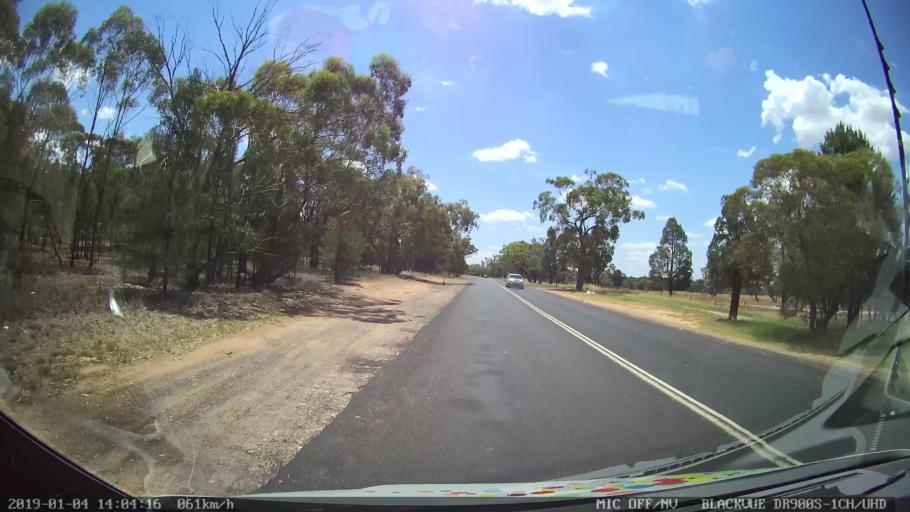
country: AU
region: New South Wales
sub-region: Dubbo Municipality
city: Dubbo
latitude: -32.2703
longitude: 148.5864
